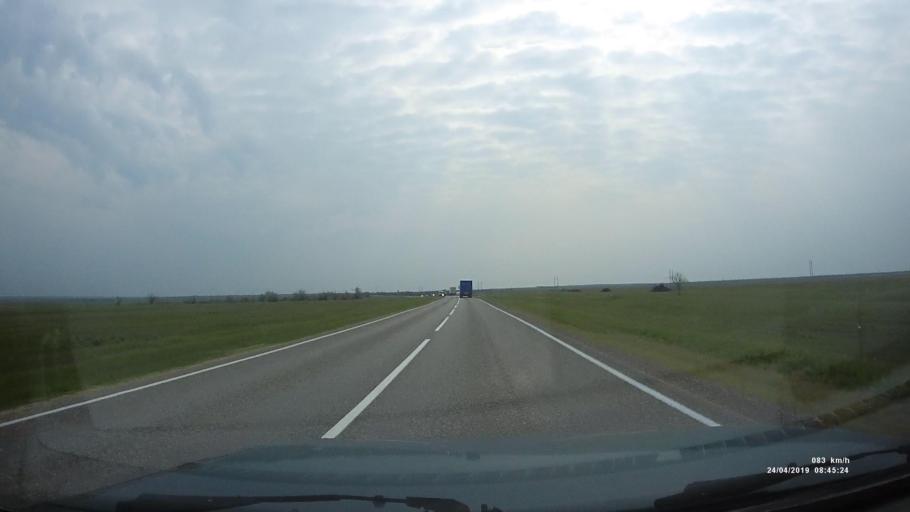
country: RU
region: Kalmykiya
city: Arshan'
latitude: 46.2362
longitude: 44.0602
